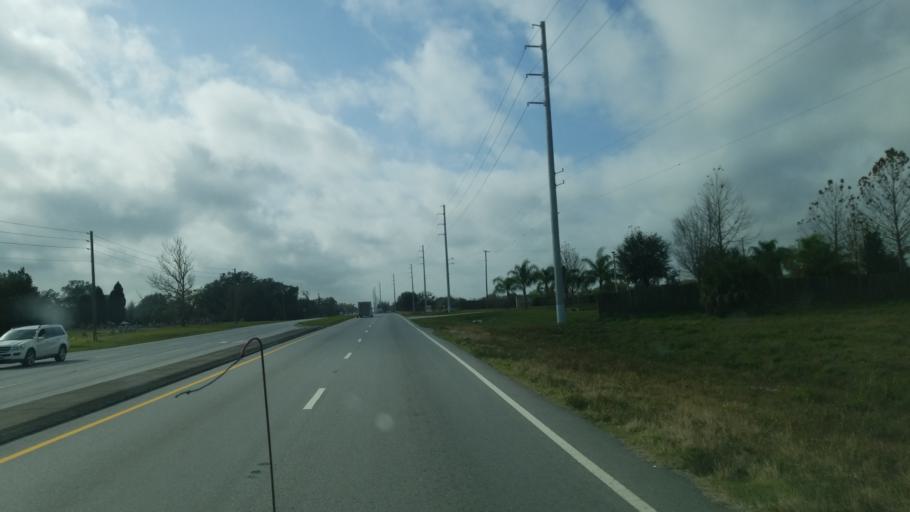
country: US
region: Florida
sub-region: Polk County
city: Winston
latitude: 27.9815
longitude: -82.0560
